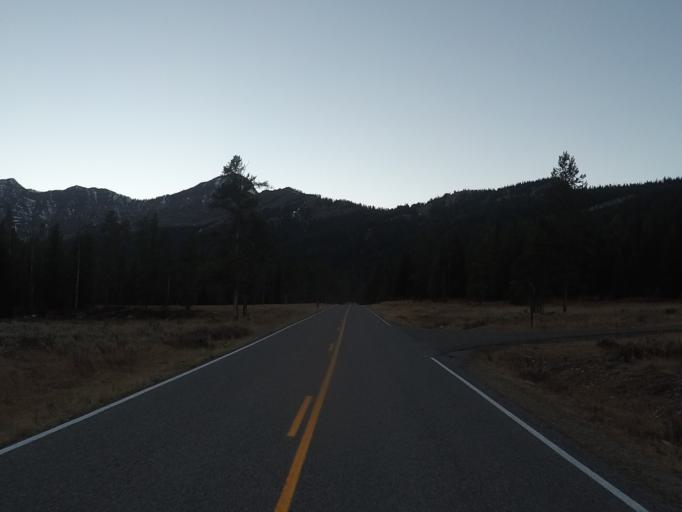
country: US
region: Montana
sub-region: Stillwater County
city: Absarokee
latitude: 45.0045
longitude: -110.0330
